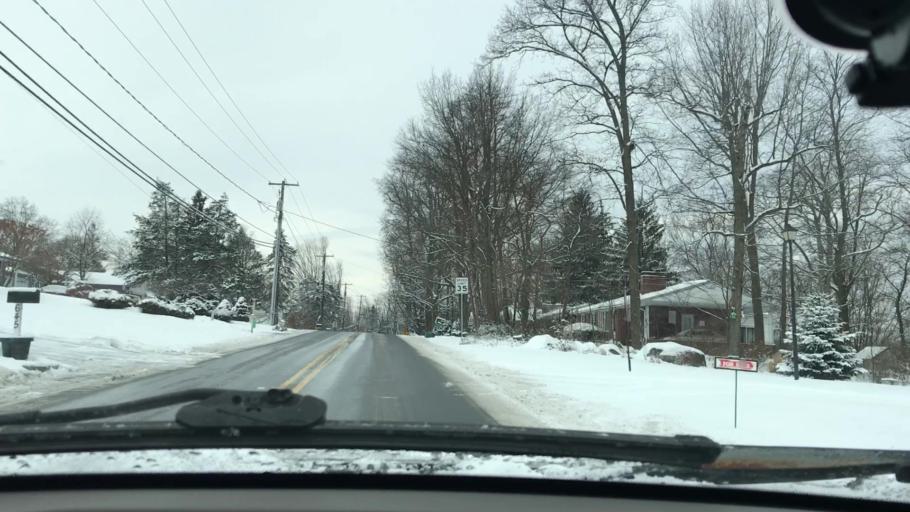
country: US
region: Pennsylvania
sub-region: Lancaster County
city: Elizabethtown
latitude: 40.1714
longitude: -76.6000
